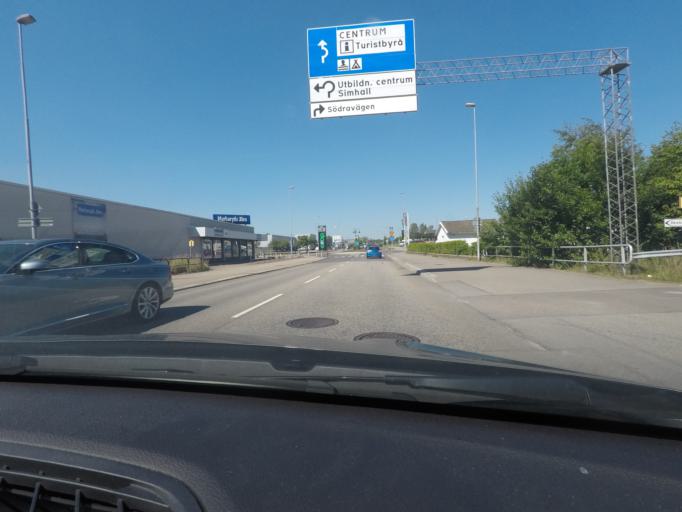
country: SE
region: Kronoberg
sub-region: Markaryds Kommun
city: Markaryd
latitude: 56.4559
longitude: 13.5944
